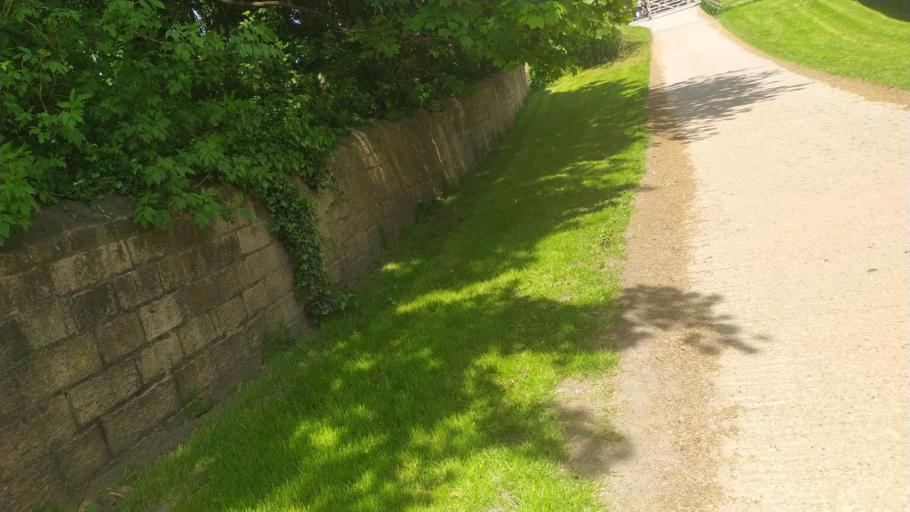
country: GB
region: England
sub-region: North Yorkshire
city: Pannal
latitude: 53.8965
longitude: -1.5357
